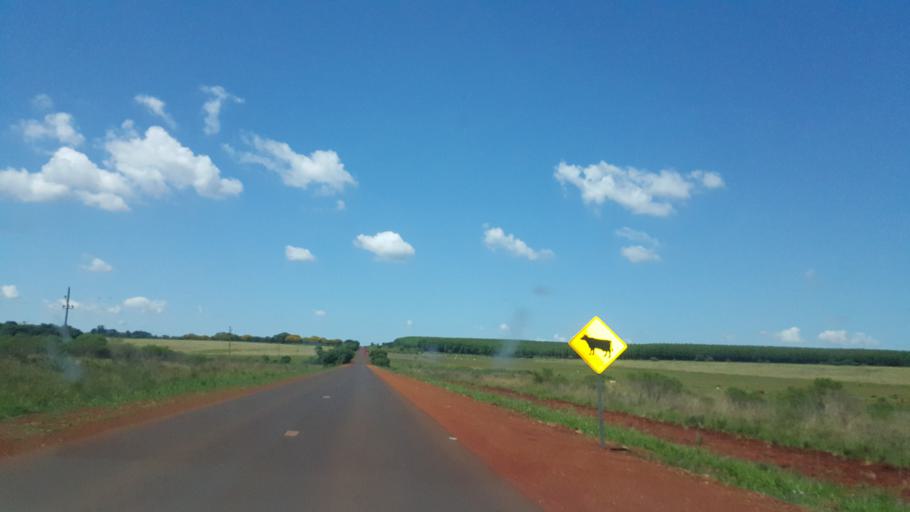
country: AR
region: Corrientes
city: Santo Tome
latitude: -28.3411
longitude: -55.9288
